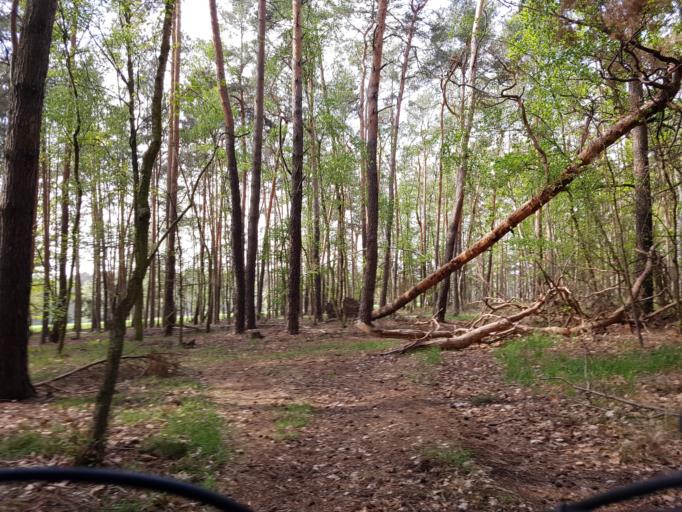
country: DE
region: Brandenburg
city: Schilda
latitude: 51.5942
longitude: 13.3714
